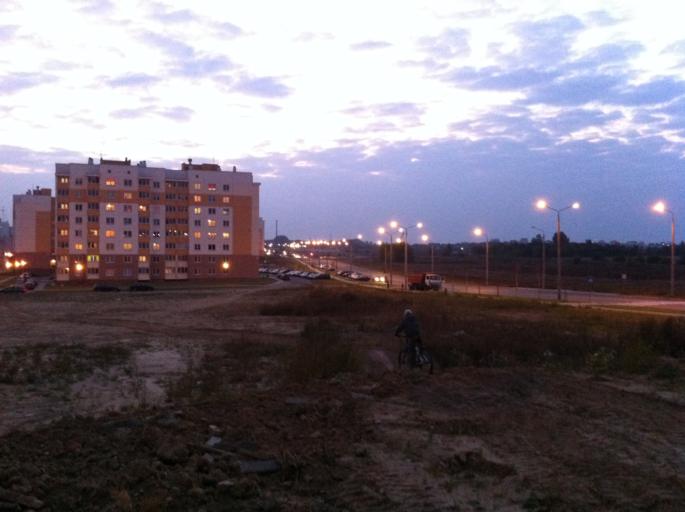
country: BY
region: Grodnenskaya
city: Hrodna
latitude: 53.7128
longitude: 23.8686
